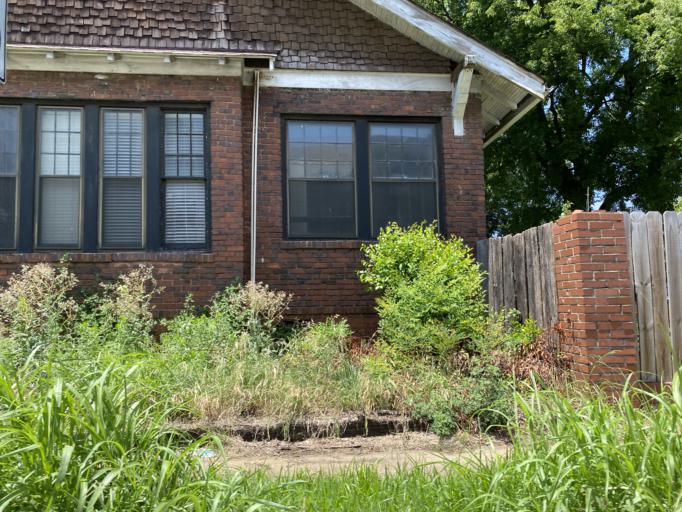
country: US
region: Alabama
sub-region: Morgan County
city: Decatur
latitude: 34.6011
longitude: -86.9802
